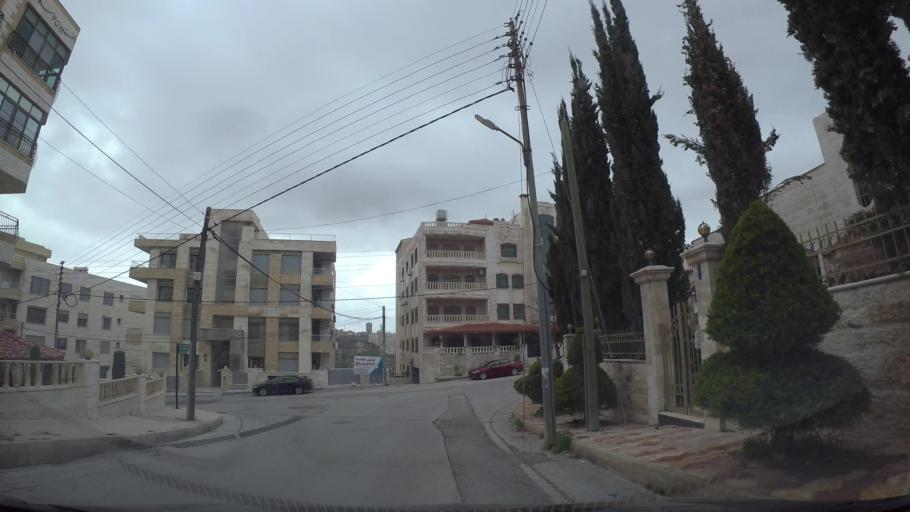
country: JO
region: Amman
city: Wadi as Sir
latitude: 31.9600
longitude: 35.8270
